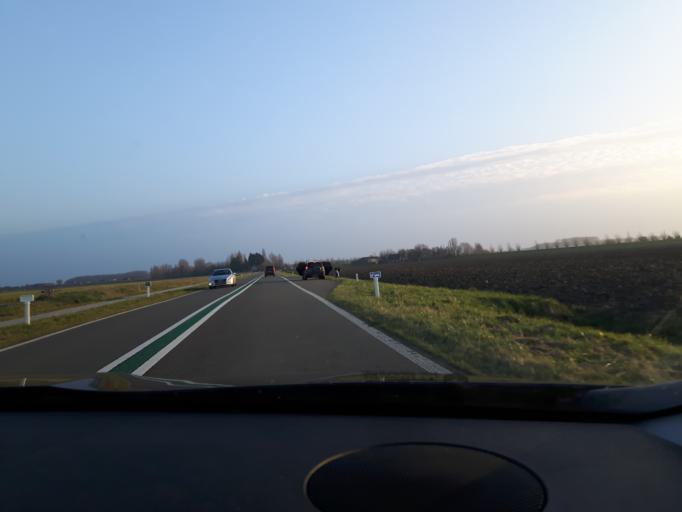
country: NL
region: Zeeland
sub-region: Gemeente Noord-Beveland
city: Kamperland
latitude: 51.5843
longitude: 3.6918
